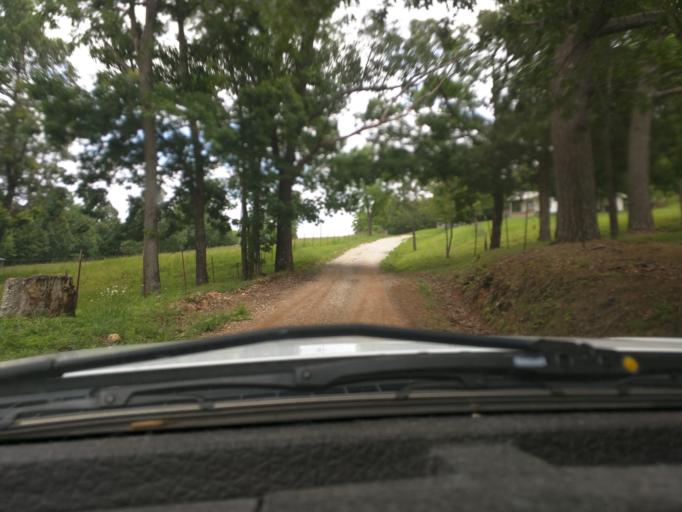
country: US
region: Arkansas
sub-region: Madison County
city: Huntsville
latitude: 35.8833
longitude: -93.5433
